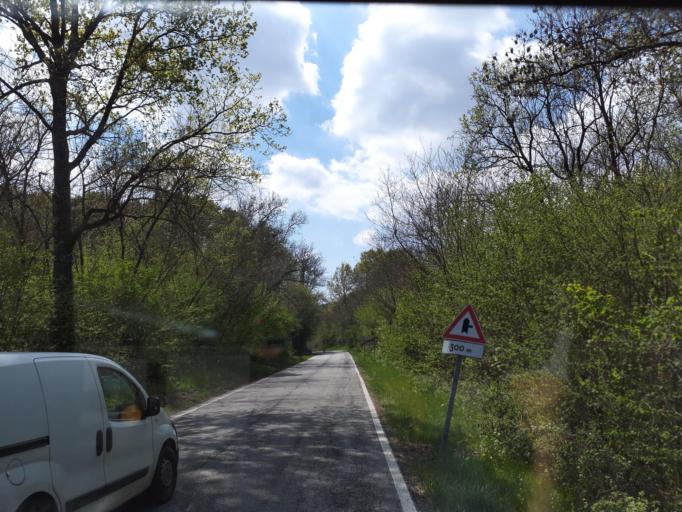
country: IT
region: Piedmont
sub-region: Provincia di Biella
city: Zubiena
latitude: 45.5057
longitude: 7.9995
